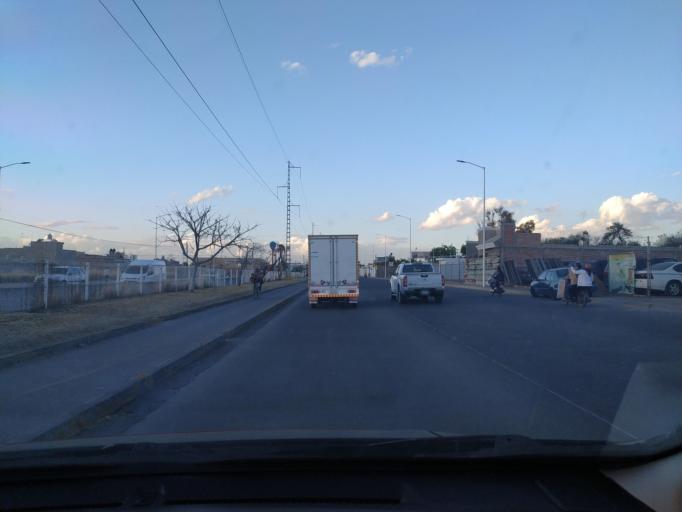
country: LA
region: Oudomxai
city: Muang La
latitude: 21.0146
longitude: 101.8697
